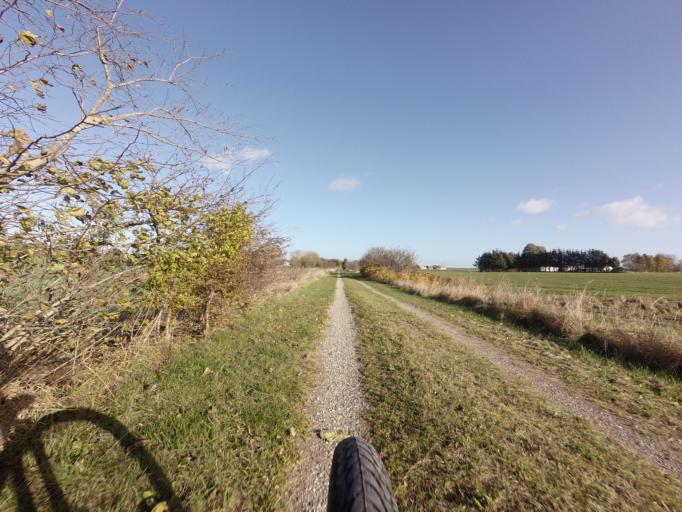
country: DK
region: Central Jutland
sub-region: Syddjurs Kommune
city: Ryomgard
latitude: 56.4319
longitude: 10.6154
